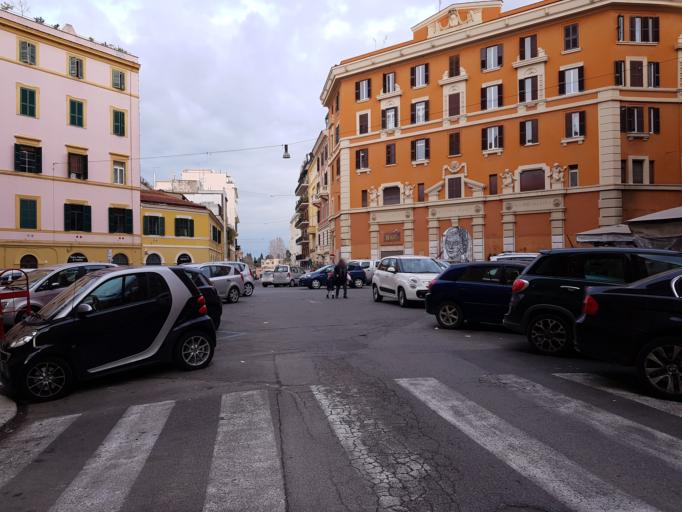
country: IT
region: Latium
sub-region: Citta metropolitana di Roma Capitale
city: Rome
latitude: 41.8986
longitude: 12.5163
